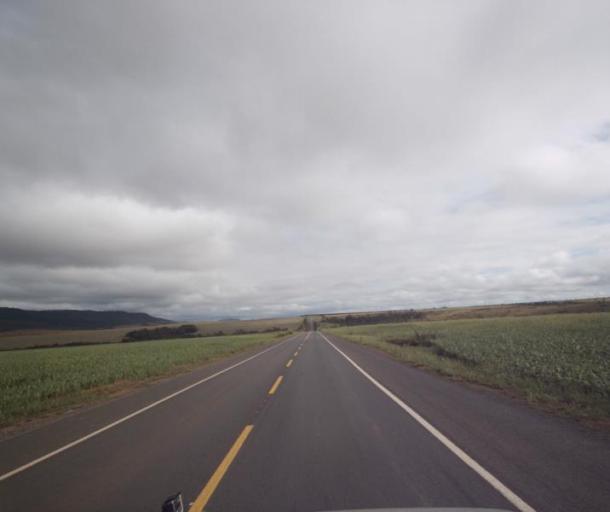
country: BR
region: Goias
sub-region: Padre Bernardo
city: Padre Bernardo
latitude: -15.4012
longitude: -48.6325
